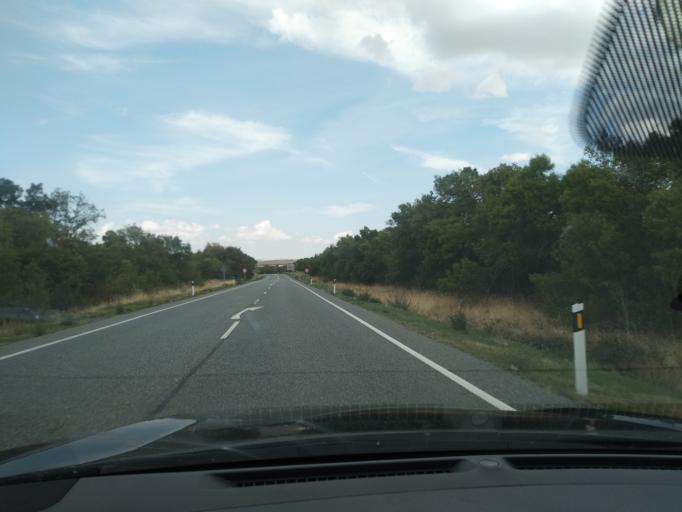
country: ES
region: Castille and Leon
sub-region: Provincia de Segovia
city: Palazuelos de Eresma
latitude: 40.8809
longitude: -4.0992
